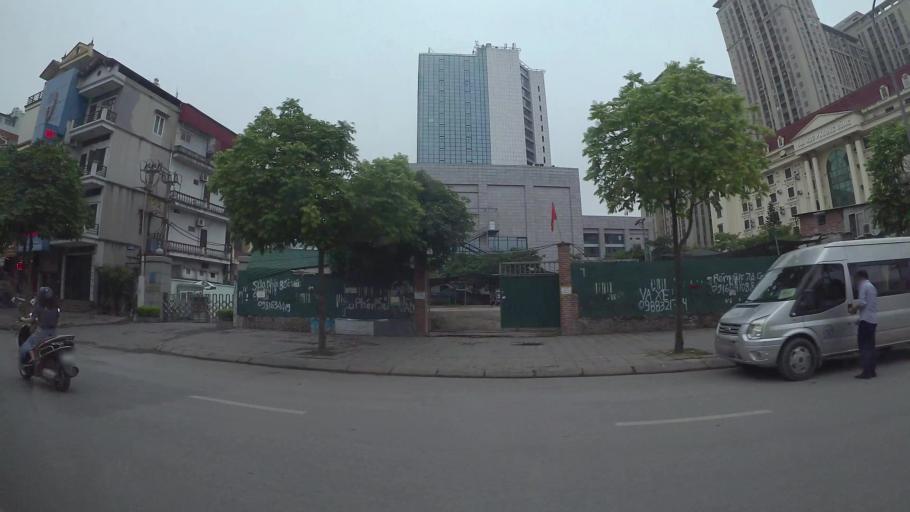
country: VN
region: Ha Noi
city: Cau Giay
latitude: 21.0158
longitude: 105.7946
